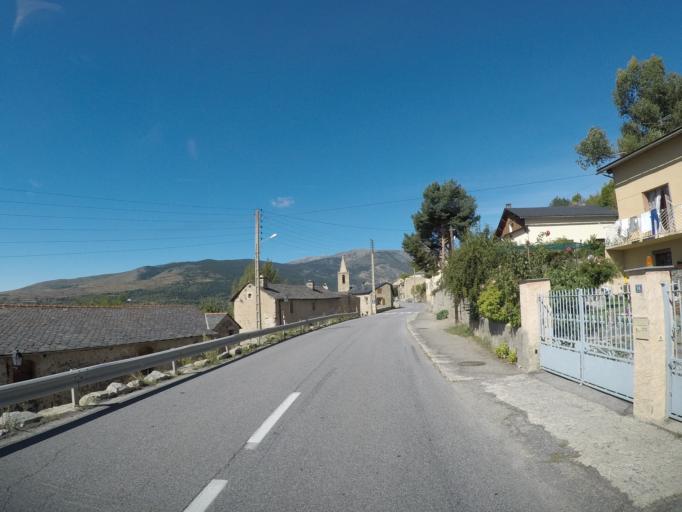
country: ES
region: Catalonia
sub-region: Provincia de Girona
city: Puigcerda
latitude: 42.4595
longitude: 1.9179
